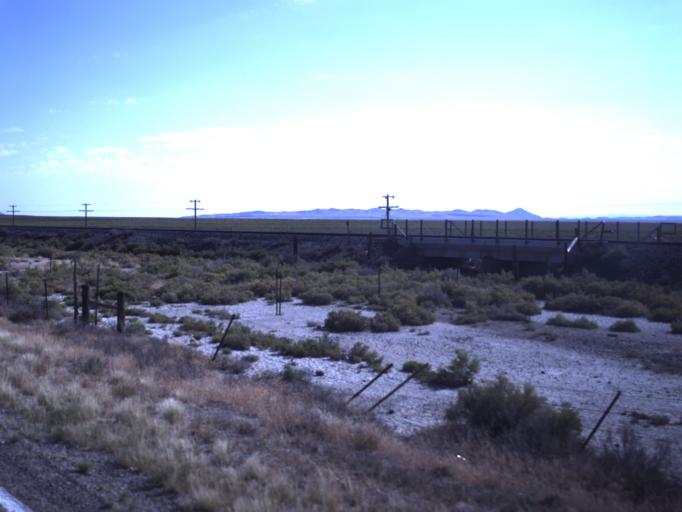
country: US
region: Utah
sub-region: Beaver County
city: Milford
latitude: 38.6130
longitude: -112.9858
